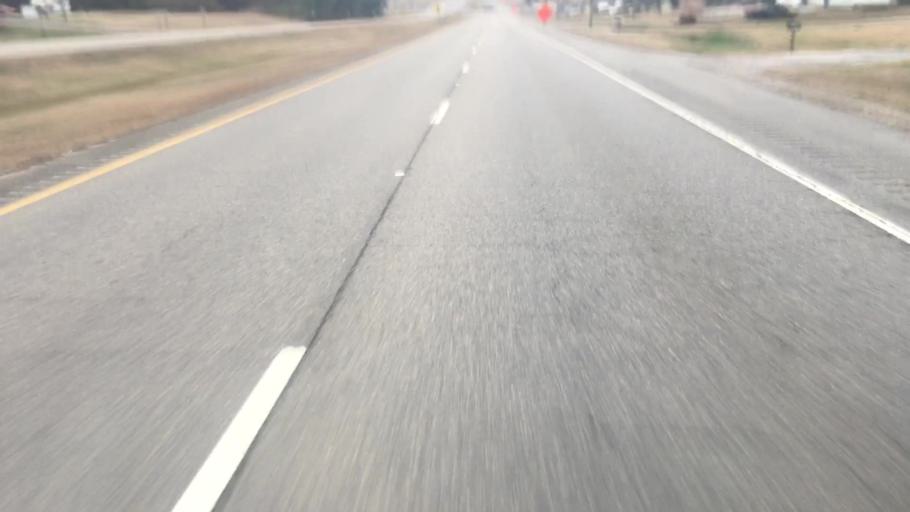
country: US
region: Alabama
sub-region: Walker County
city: Sumiton
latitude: 33.7609
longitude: -87.0672
